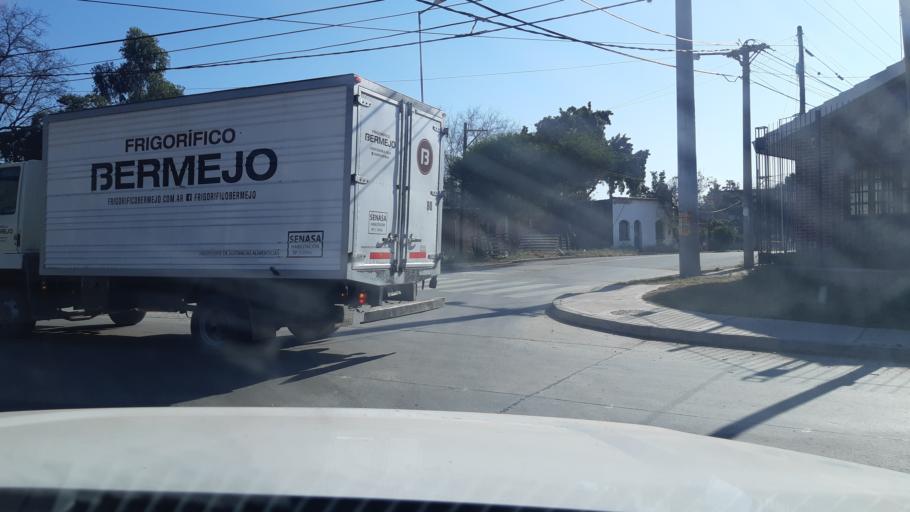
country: AR
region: Jujuy
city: Palpala
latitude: -24.2286
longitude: -65.2401
